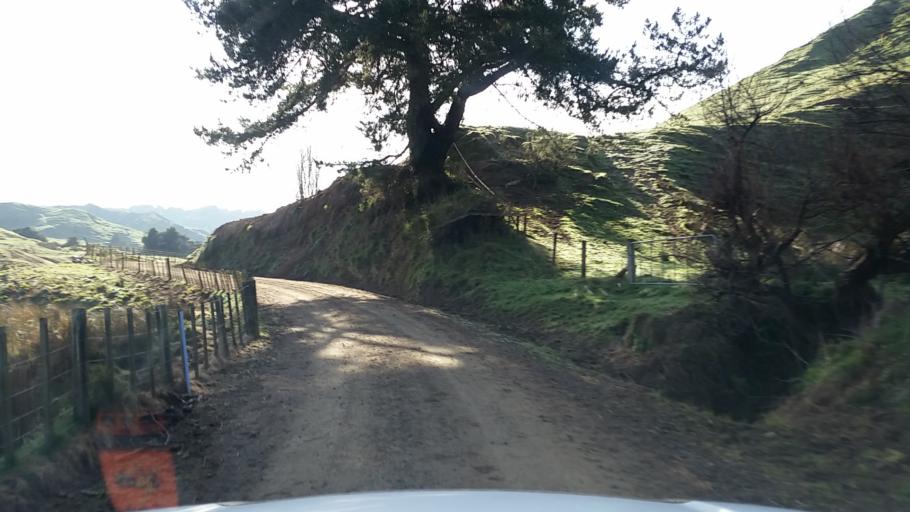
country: NZ
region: Taranaki
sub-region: South Taranaki District
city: Eltham
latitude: -39.3186
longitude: 174.5325
